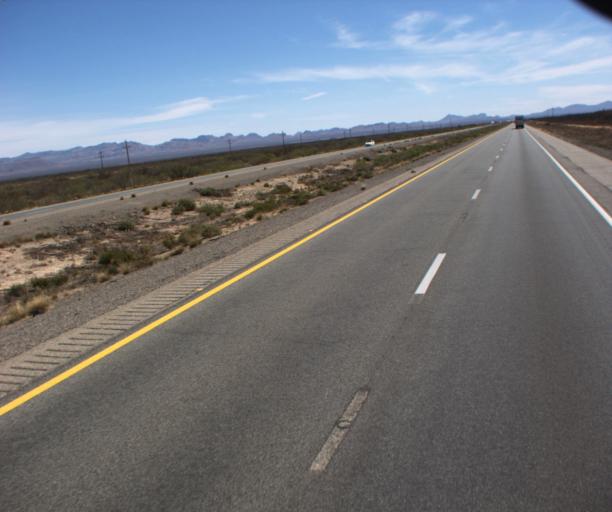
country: US
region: Arizona
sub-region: Cochise County
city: Willcox
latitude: 32.2833
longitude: -109.2935
